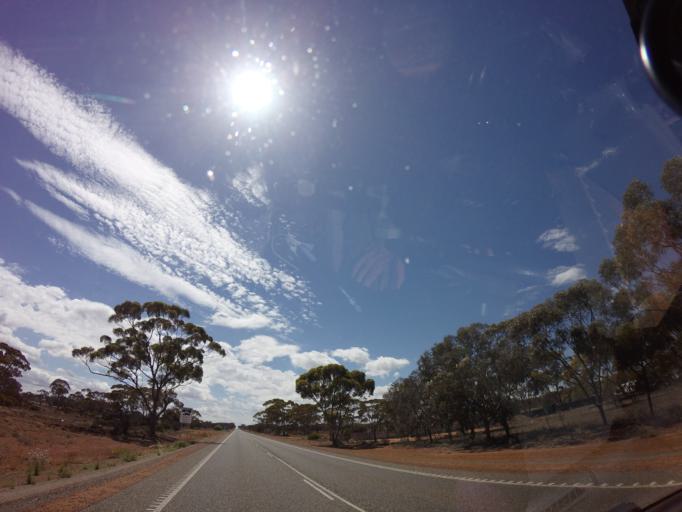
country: AU
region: Western Australia
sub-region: Kalgoorlie/Boulder
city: Boulder
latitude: -30.9546
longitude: 121.1456
